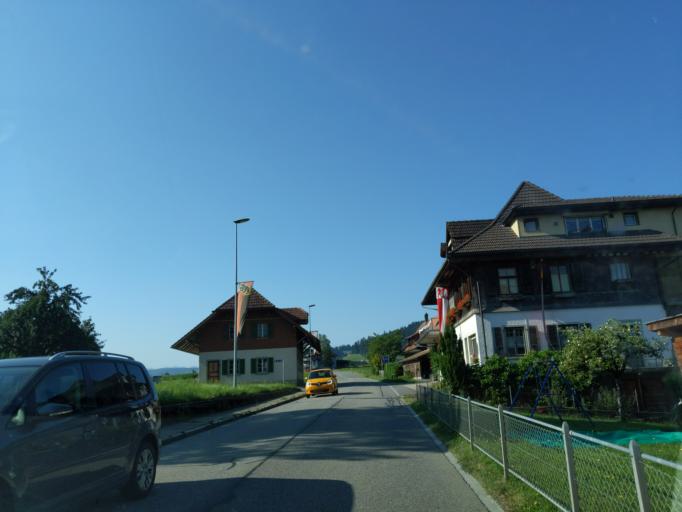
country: CH
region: Bern
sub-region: Emmental District
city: Lauperswil
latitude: 46.9649
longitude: 7.7409
